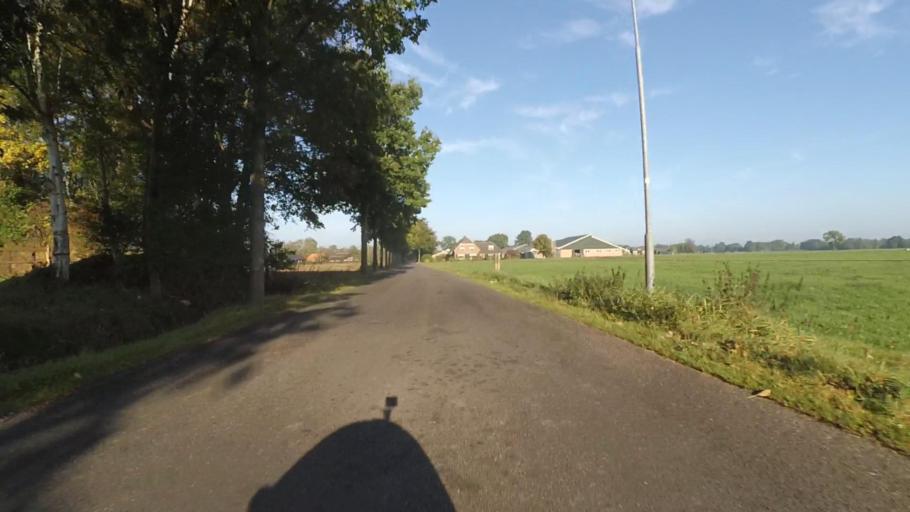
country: NL
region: Gelderland
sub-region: Gemeente Epe
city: Vaassen
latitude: 52.2928
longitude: 5.9559
